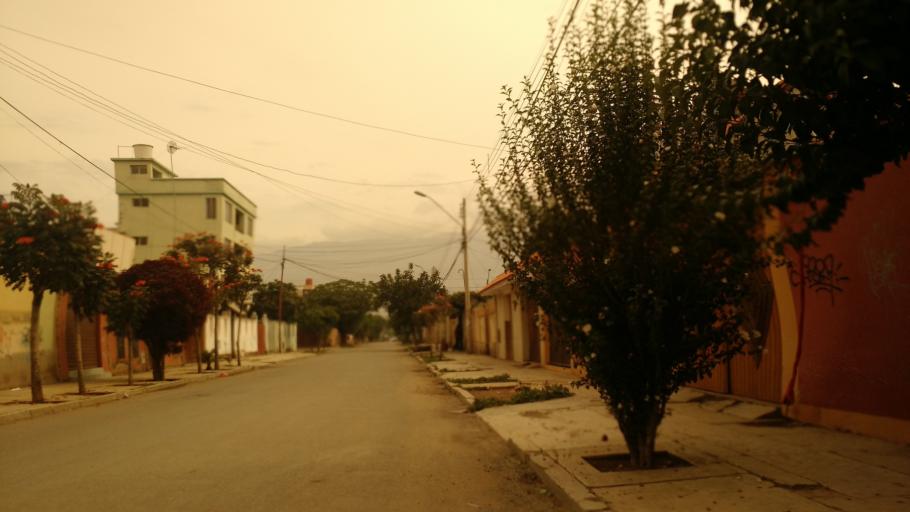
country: BO
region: Cochabamba
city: Cochabamba
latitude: -17.4235
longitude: -66.1558
